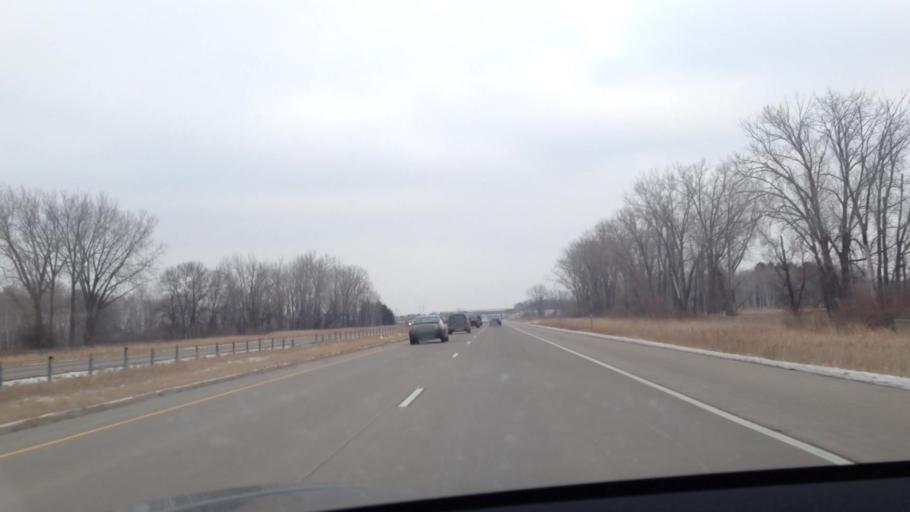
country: US
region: Minnesota
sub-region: Anoka County
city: Lino Lakes
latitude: 45.1900
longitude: -93.0822
